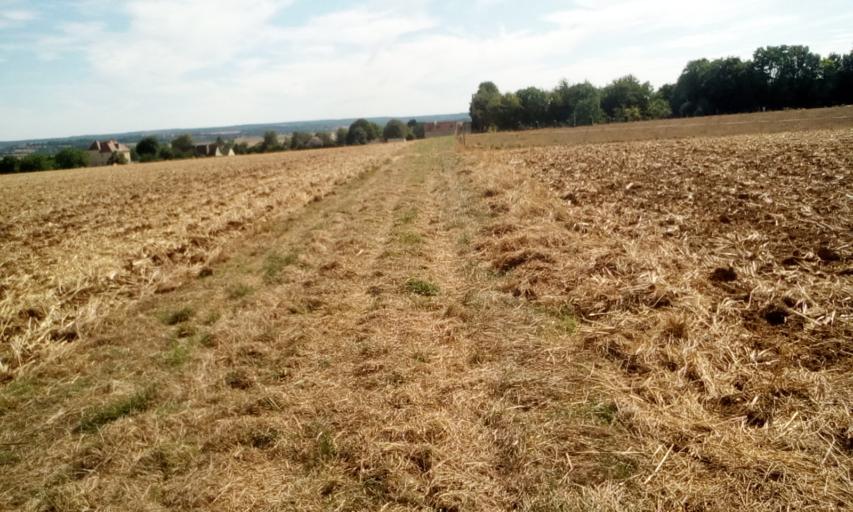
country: FR
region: Lower Normandy
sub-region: Departement du Calvados
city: Bully
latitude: 49.1147
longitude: -0.4321
